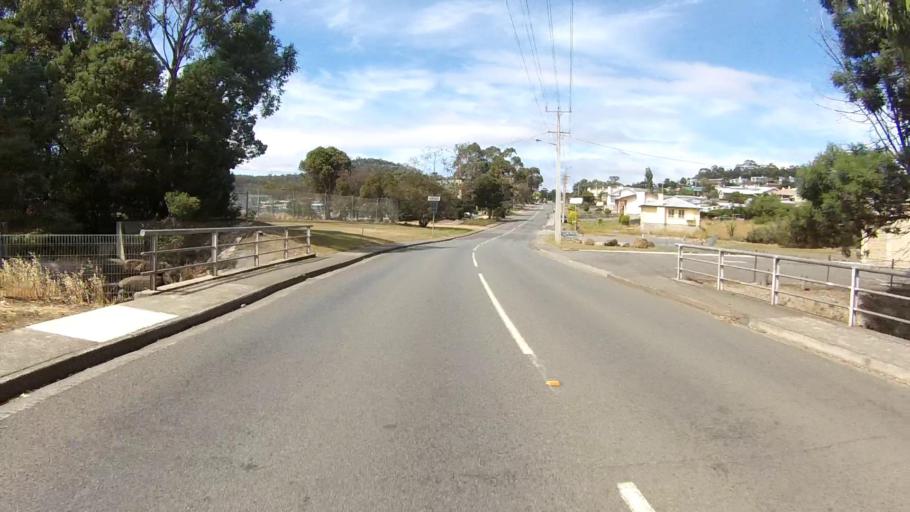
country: AU
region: Tasmania
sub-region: Clarence
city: Lindisfarne
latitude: -42.8101
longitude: 147.3511
